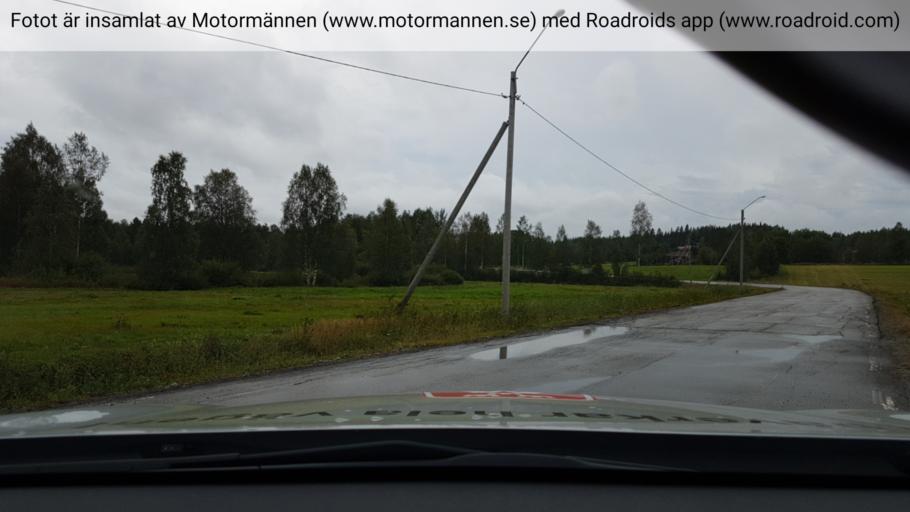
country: SE
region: Vaesterbotten
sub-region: Skelleftea Kommun
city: Burtraesk
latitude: 64.3116
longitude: 20.6583
